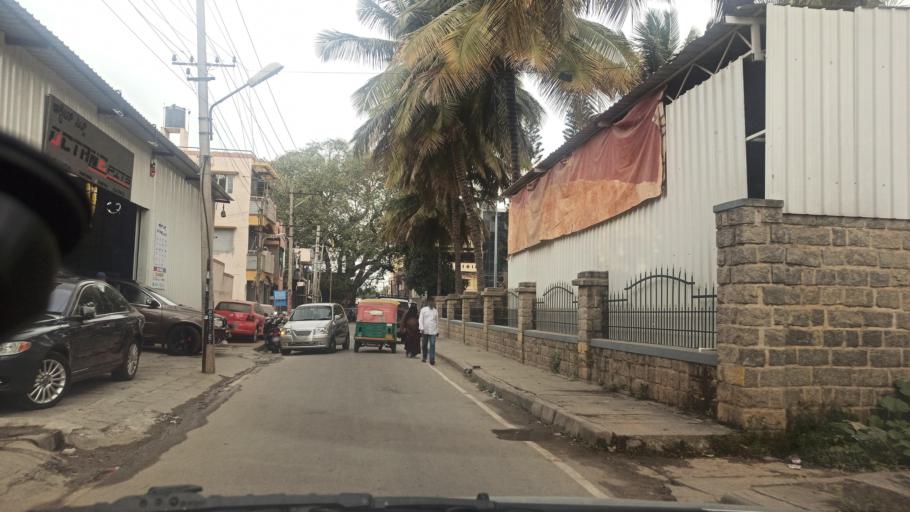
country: IN
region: Karnataka
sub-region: Bangalore Urban
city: Yelahanka
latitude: 13.0386
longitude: 77.6050
